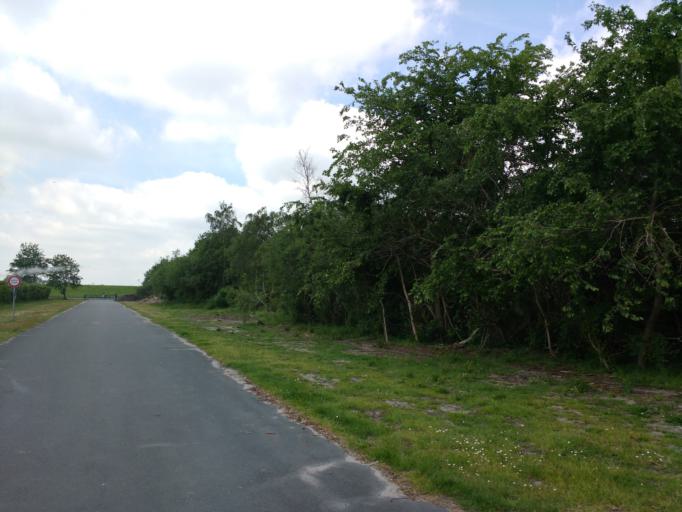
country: DE
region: Lower Saxony
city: Schillig
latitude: 53.6458
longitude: 8.0348
